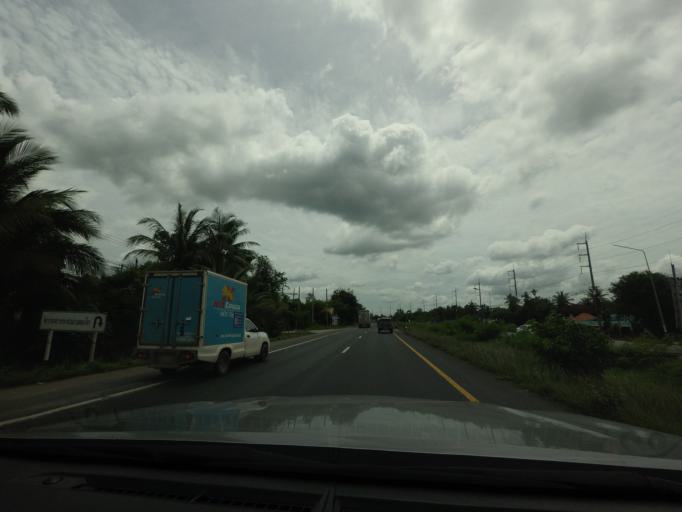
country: TH
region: Surat Thani
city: Tha Chang
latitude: 9.1935
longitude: 99.1413
